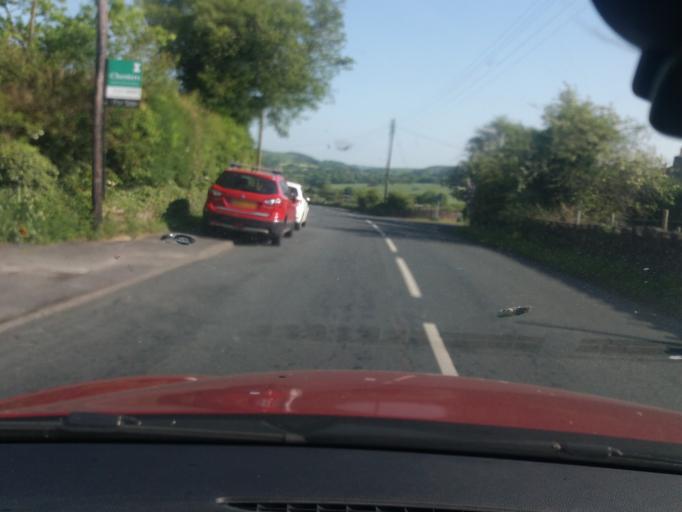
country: GB
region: England
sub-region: Lancashire
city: Adlington
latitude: 53.6267
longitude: -2.5882
